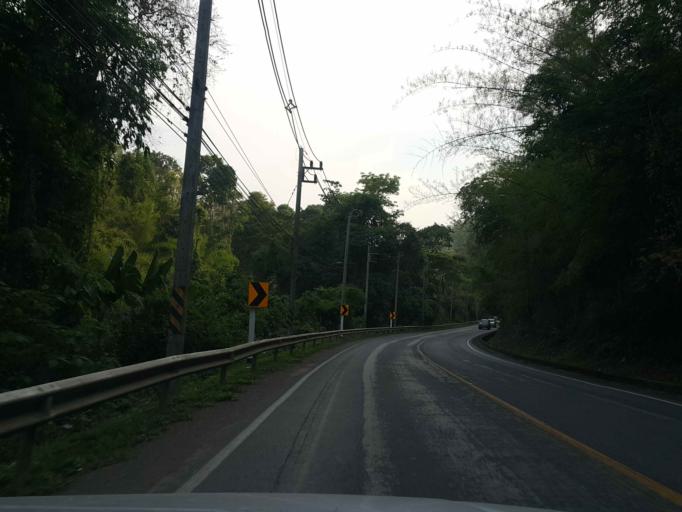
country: TH
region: Chiang Mai
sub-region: Amphoe Chiang Dao
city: Chiang Dao
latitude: 19.2727
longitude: 98.9715
